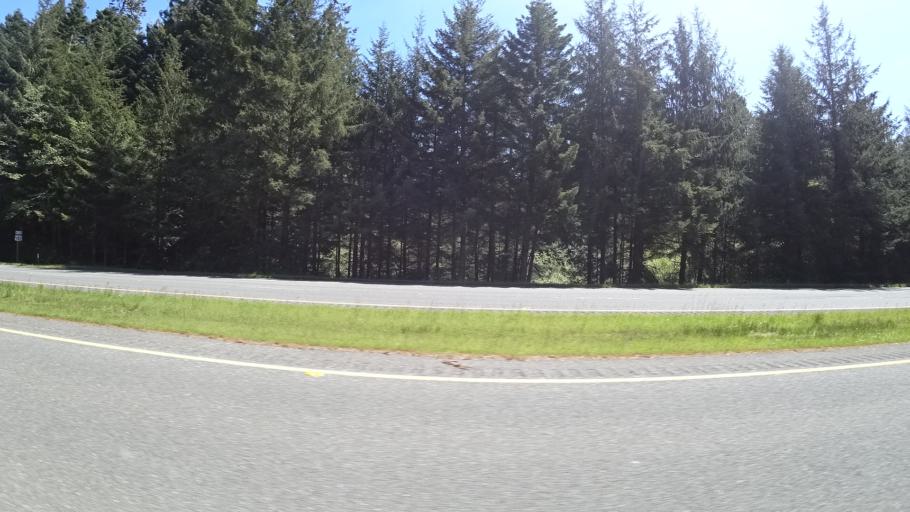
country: US
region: California
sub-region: Humboldt County
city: Westhaven-Moonstone
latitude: 41.1029
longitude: -124.1545
